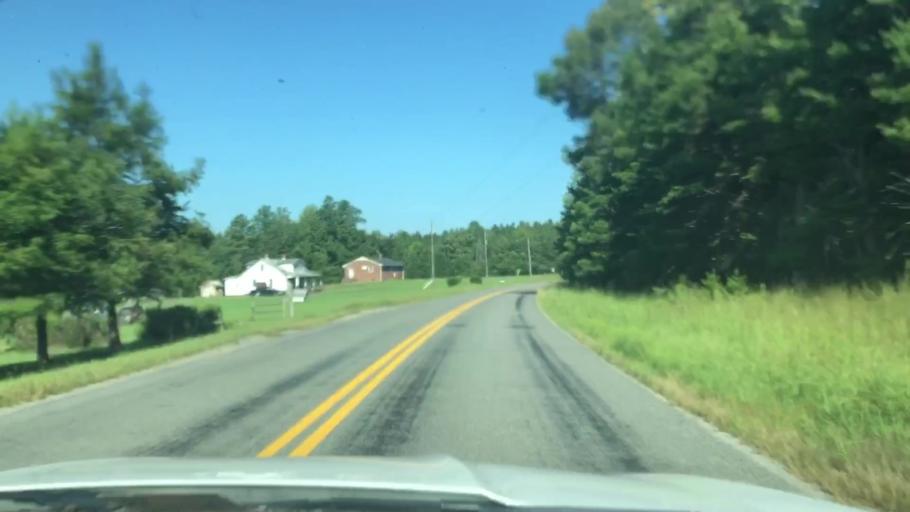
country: US
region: Virginia
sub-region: New Kent County
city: New Kent
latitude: 37.4856
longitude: -76.9311
